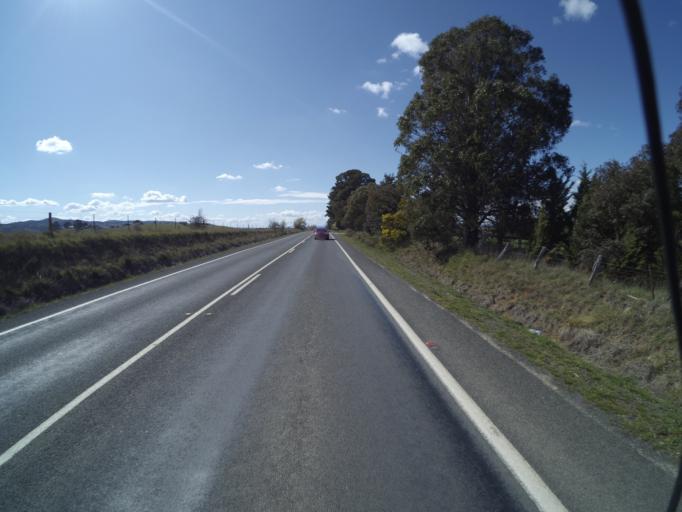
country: AU
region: New South Wales
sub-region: Palerang
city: Bungendore
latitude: -35.2903
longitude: 149.4205
